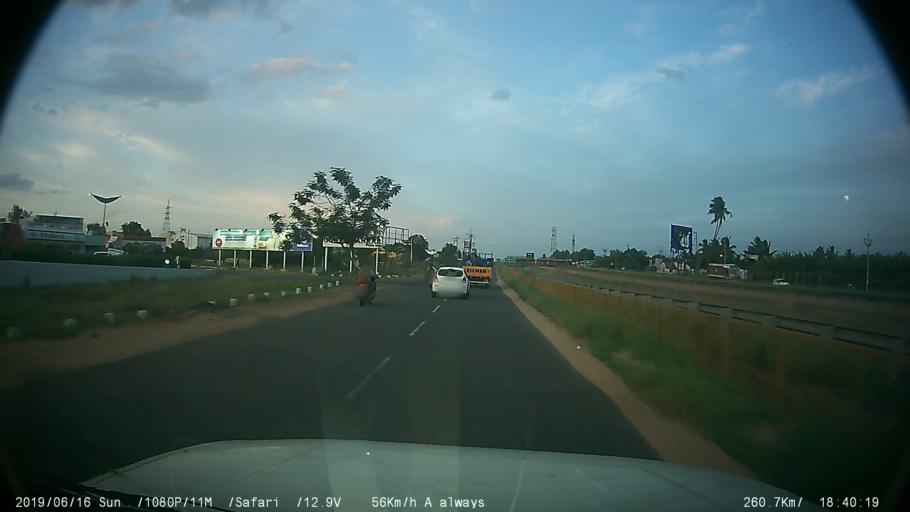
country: IN
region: Tamil Nadu
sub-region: Coimbatore
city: Sulur
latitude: 11.0898
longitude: 77.1345
